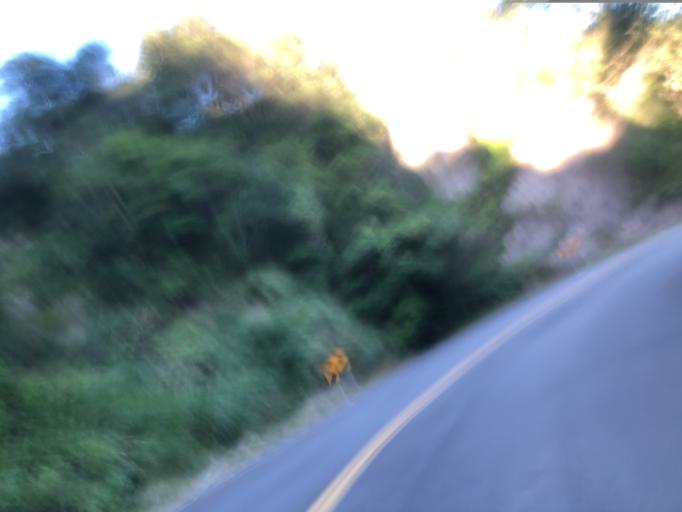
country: TW
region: Taiwan
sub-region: Miaoli
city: Miaoli
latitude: 24.5809
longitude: 120.9316
